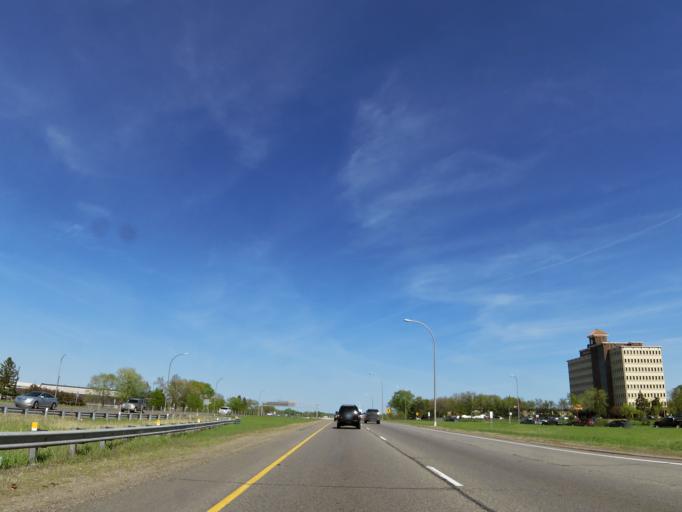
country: US
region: Minnesota
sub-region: Ramsey County
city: Roseville
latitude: 45.0100
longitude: -93.1757
